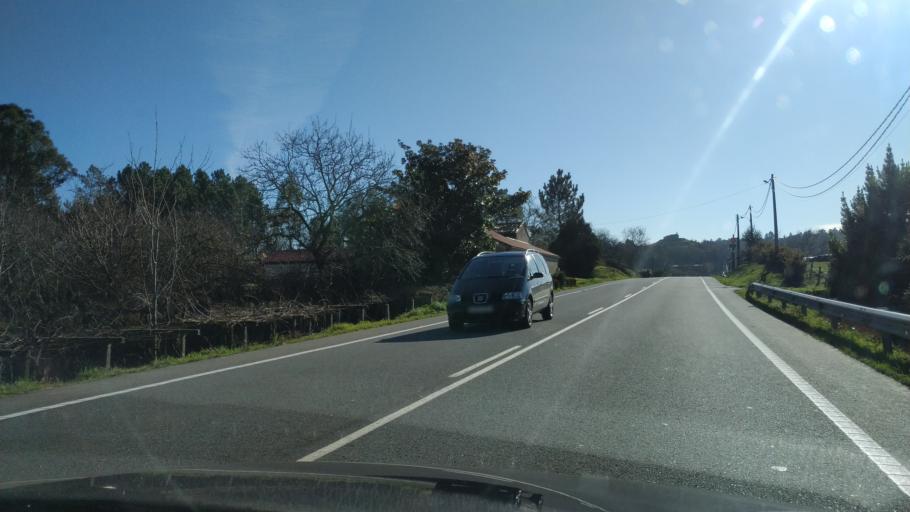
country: ES
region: Galicia
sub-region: Provincia da Coruna
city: Ribeira
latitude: 42.7510
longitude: -8.3504
